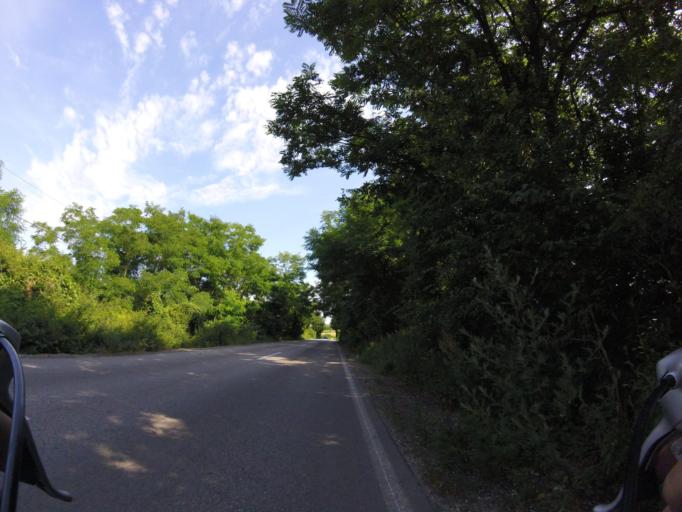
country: HU
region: Komarom-Esztergom
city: Tatabanya
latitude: 47.5533
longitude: 18.3801
